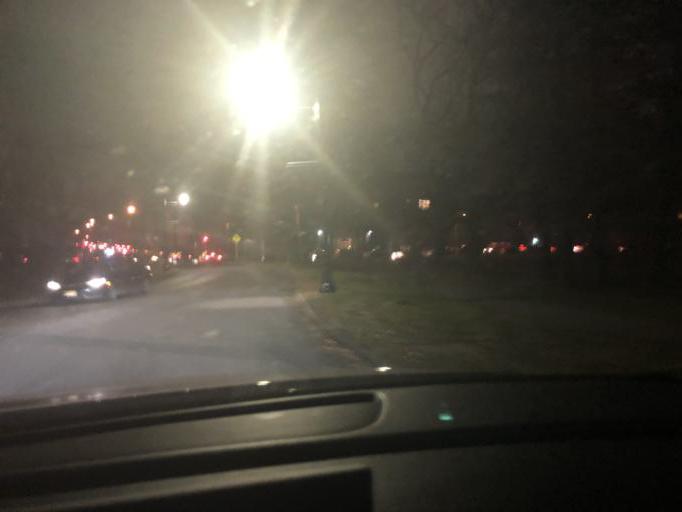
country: US
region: New Jersey
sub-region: Hudson County
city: East Newark
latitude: 40.7645
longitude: -74.1779
